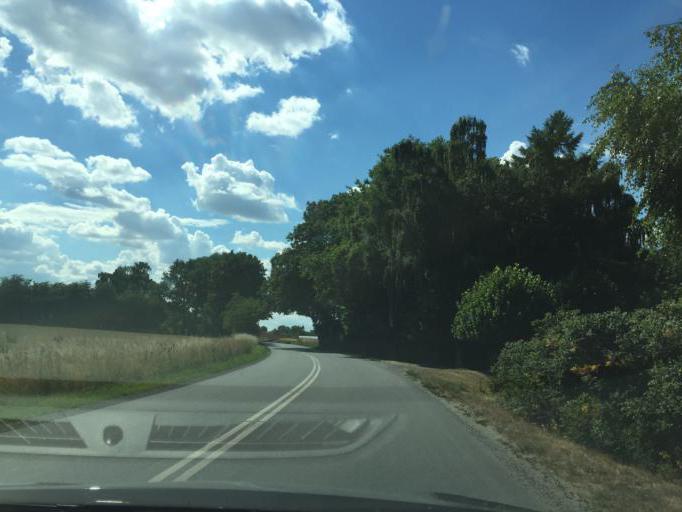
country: DK
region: South Denmark
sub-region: Odense Kommune
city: Bellinge
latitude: 55.3132
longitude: 10.3277
